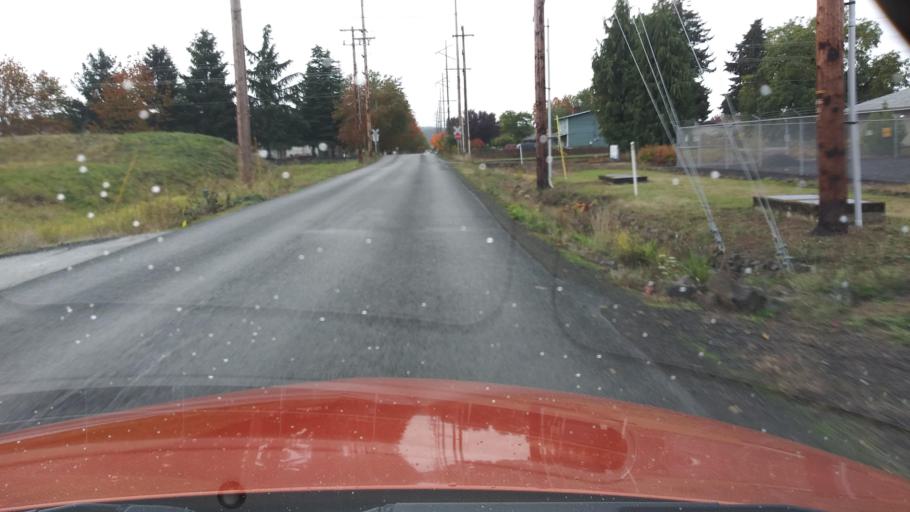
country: US
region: Oregon
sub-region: Washington County
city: Forest Grove
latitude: 45.5248
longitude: -123.0880
